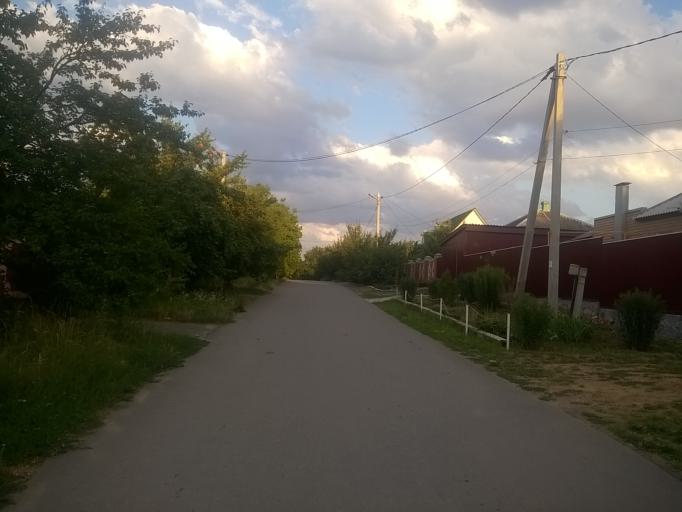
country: RU
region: Rostov
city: Donetsk
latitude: 48.3366
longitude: 39.9544
